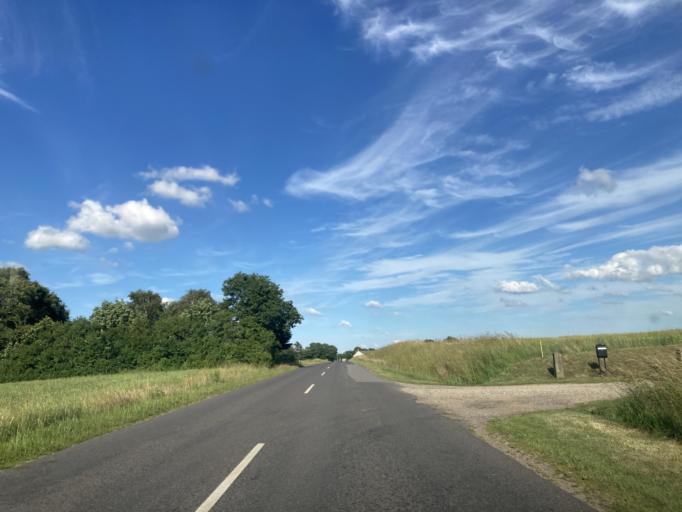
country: DK
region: South Denmark
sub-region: Kolding Kommune
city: Lunderskov
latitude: 55.4858
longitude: 9.3423
